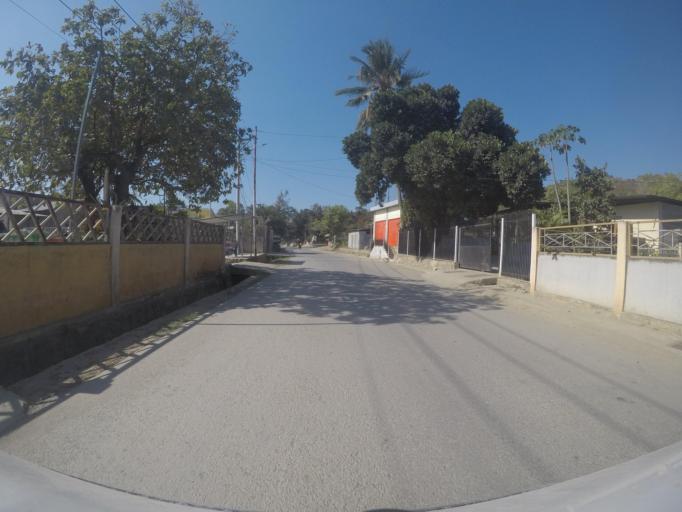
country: TL
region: Dili
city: Dili
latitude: -8.5733
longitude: 125.5426
